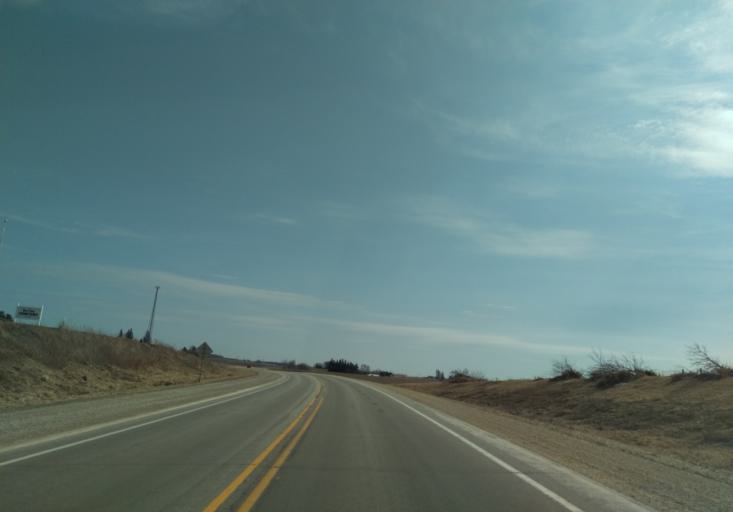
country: US
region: Iowa
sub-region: Winneshiek County
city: Decorah
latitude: 43.4541
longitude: -91.8685
